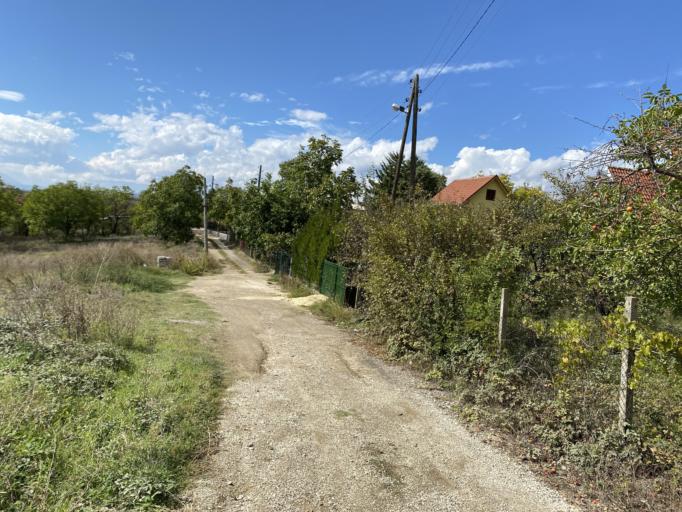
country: MK
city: Radishani
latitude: 42.0829
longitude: 21.4520
